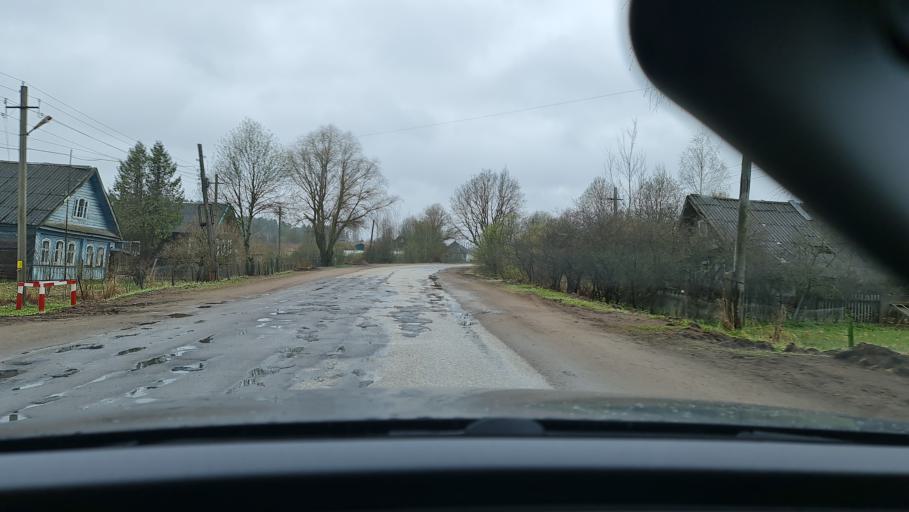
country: RU
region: Novgorod
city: Valday
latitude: 58.0359
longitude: 32.9450
